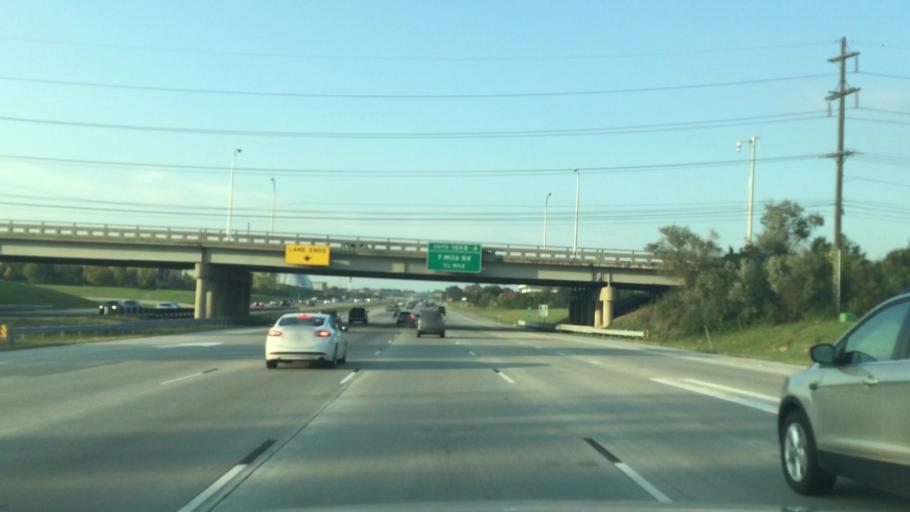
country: US
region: Michigan
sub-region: Wayne County
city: Plymouth
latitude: 42.4098
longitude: -83.4235
